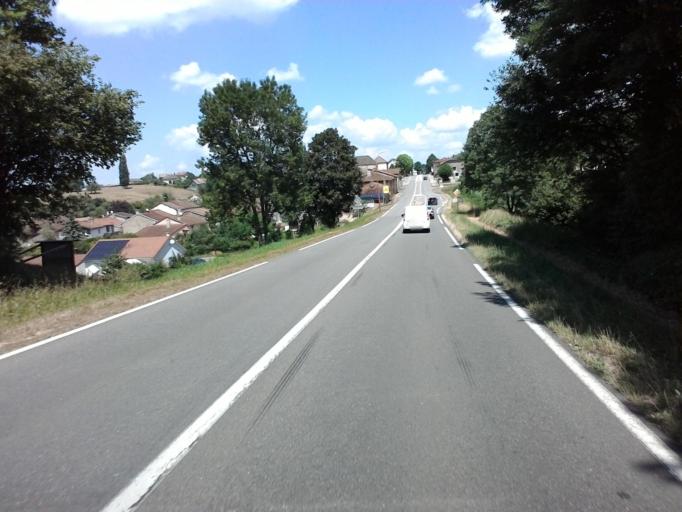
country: FR
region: Franche-Comte
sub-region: Departement du Jura
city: Saint-Amour
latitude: 46.4653
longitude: 5.3579
